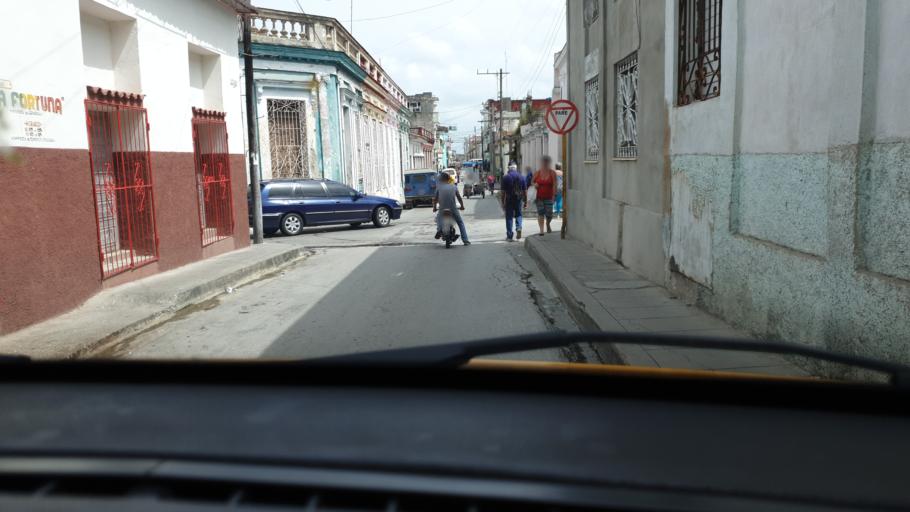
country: CU
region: Villa Clara
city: Santa Clara
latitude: 22.4054
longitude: -79.9666
